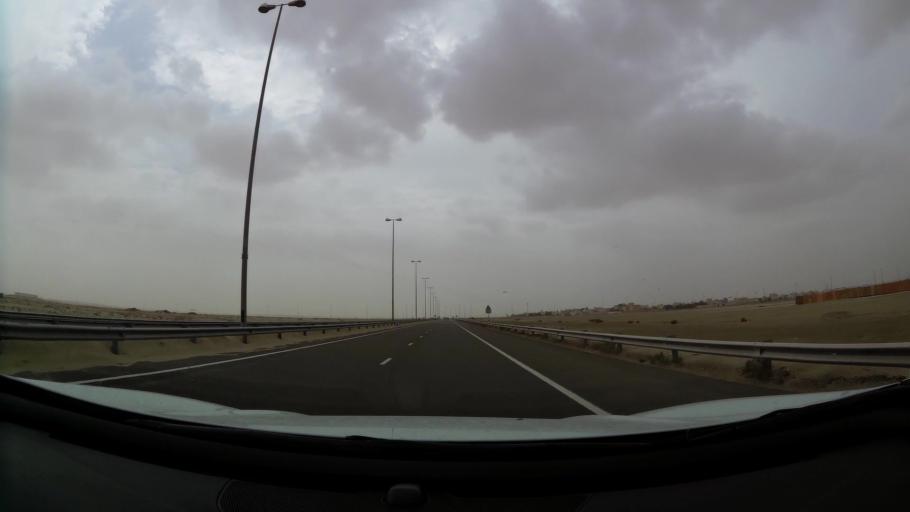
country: AE
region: Abu Dhabi
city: Abu Dhabi
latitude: 24.3648
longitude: 54.6696
